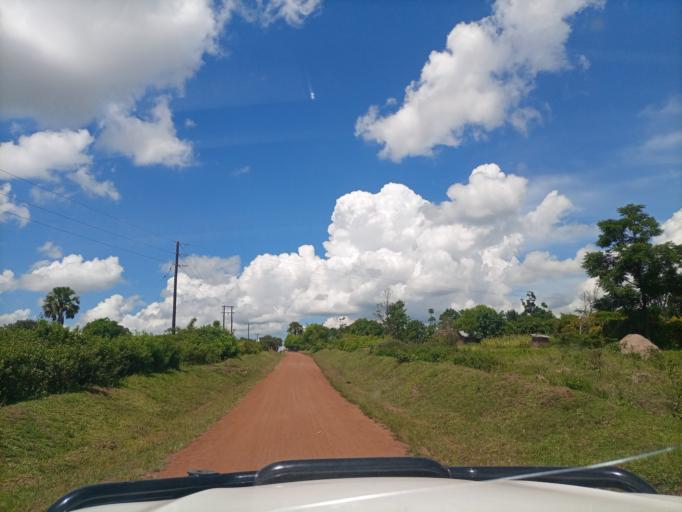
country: UG
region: Eastern Region
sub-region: Tororo District
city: Tororo
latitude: 0.6947
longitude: 34.0113
